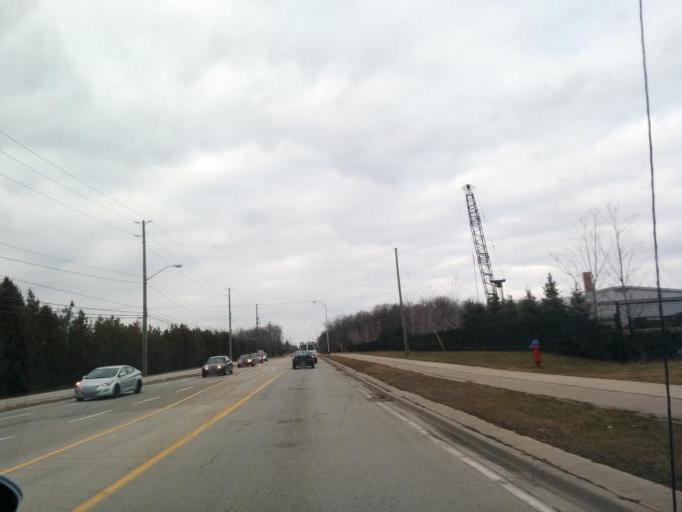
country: CA
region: Ontario
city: Oakville
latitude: 43.3855
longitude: -79.7337
